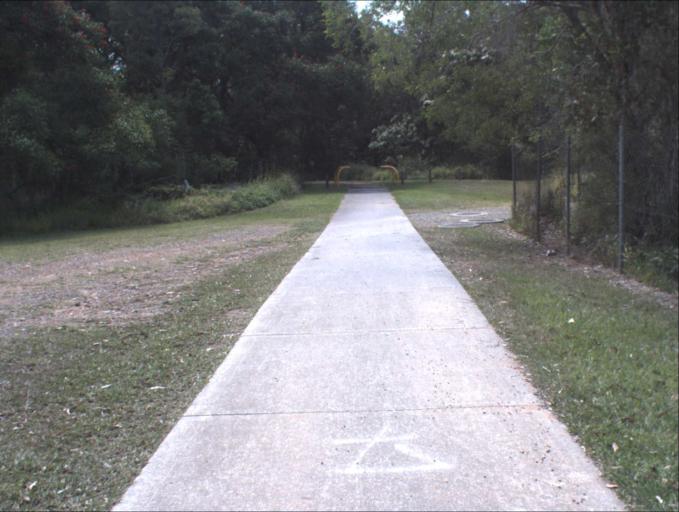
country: AU
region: Queensland
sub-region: Logan
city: Logan City
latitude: -27.6529
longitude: 153.1251
